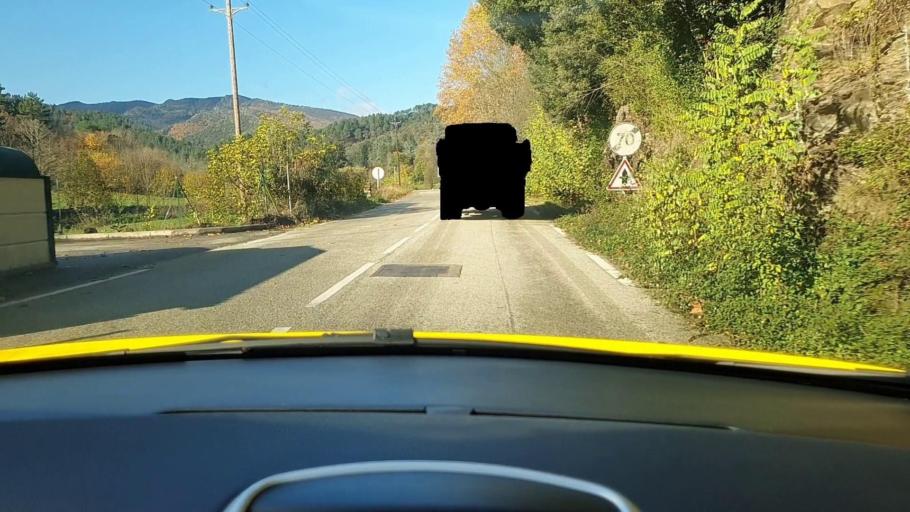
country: FR
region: Languedoc-Roussillon
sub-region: Departement du Gard
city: Valleraugue
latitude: 44.1394
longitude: 3.7213
